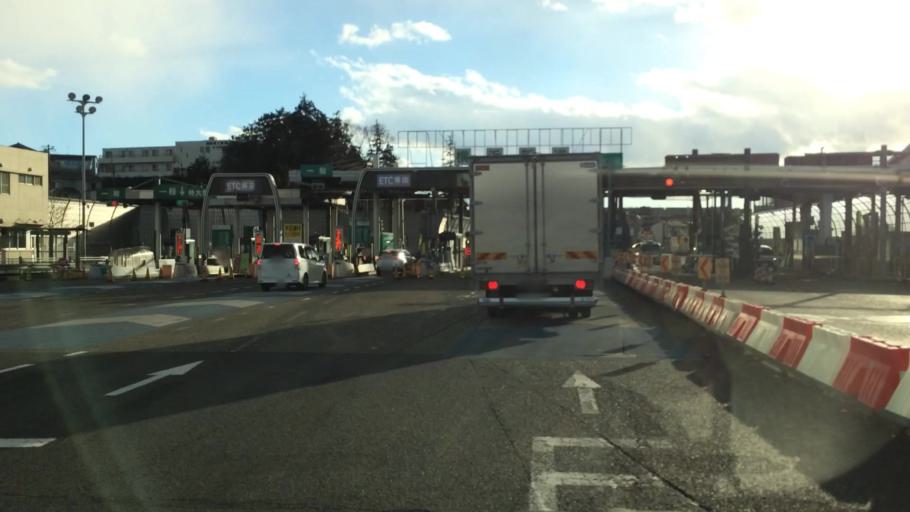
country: JP
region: Kanagawa
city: Yokohama
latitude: 35.4234
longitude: 139.5397
